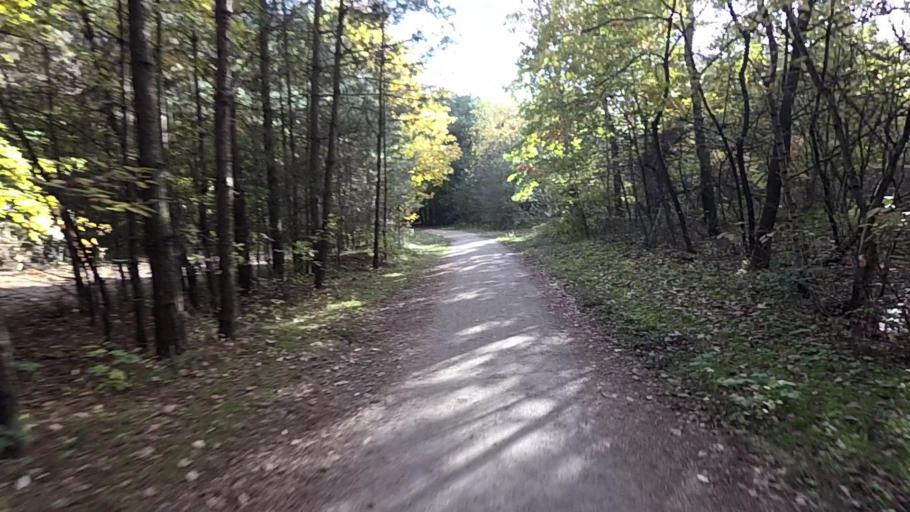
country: NL
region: North Holland
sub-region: Gemeente Laren
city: Laren
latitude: 52.2594
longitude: 5.2022
